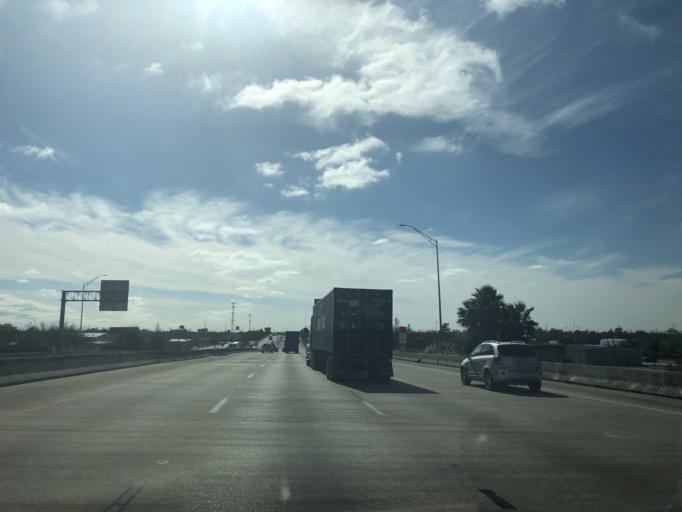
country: US
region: Texas
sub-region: Harris County
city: La Porte
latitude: 29.6724
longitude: -95.0298
